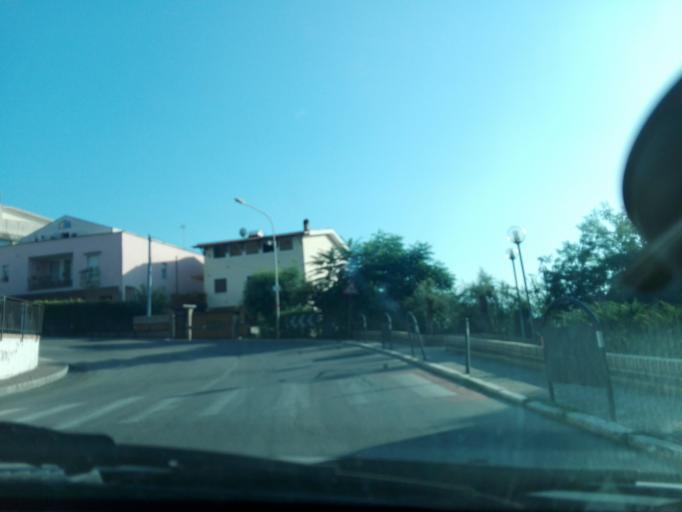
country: IT
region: Abruzzo
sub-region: Provincia di Pescara
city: Cappelle sul Tavo
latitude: 42.4647
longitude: 14.1032
